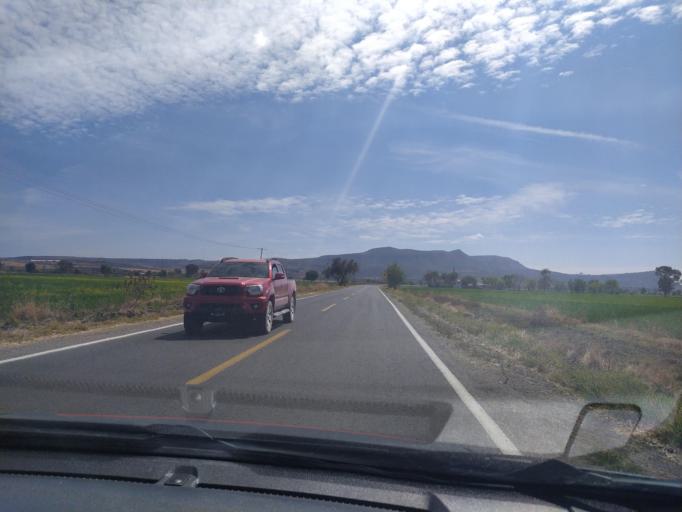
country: MX
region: Guanajuato
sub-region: San Francisco del Rincon
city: San Ignacio de Hidalgo
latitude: 20.8509
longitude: -101.8530
